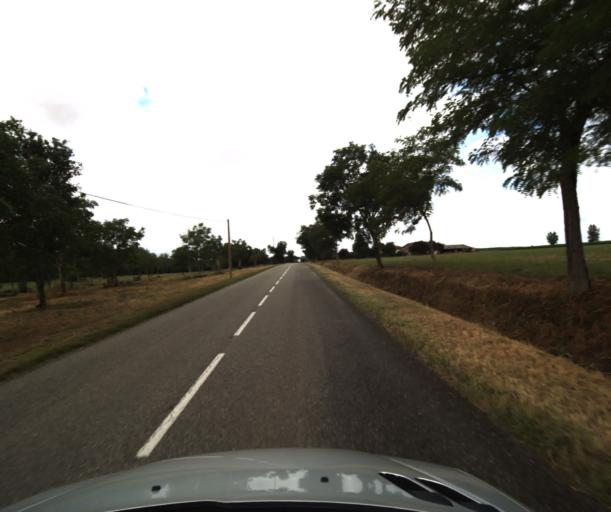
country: FR
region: Midi-Pyrenees
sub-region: Departement du Tarn-et-Garonne
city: Saint-Nicolas-de-la-Grave
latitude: 44.0272
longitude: 1.0287
